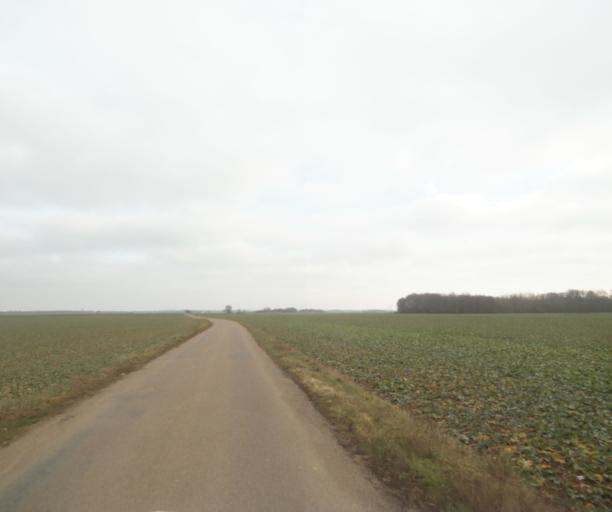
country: FR
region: Champagne-Ardenne
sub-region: Departement de la Haute-Marne
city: Villiers-en-Lieu
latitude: 48.6706
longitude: 4.8416
